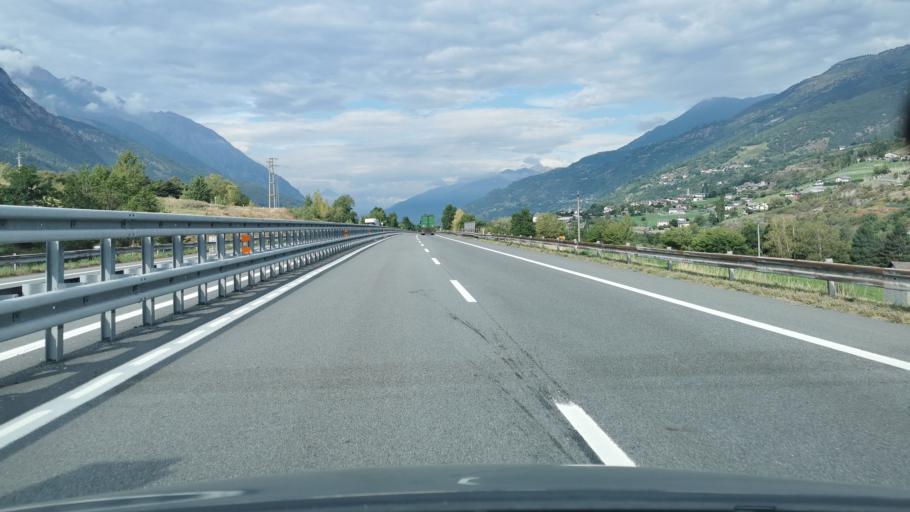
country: IT
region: Aosta Valley
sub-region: Valle d'Aosta
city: Chambave
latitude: 45.7419
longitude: 7.5401
